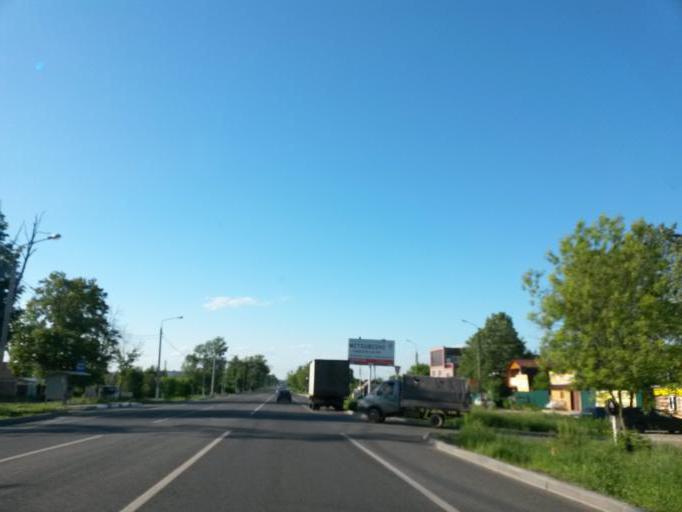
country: RU
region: Moskovskaya
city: L'vovskiy
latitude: 55.3222
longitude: 37.5286
